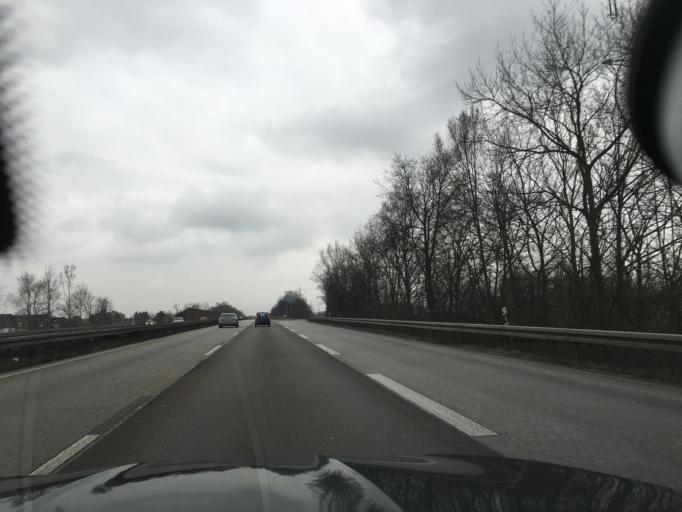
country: DE
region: North Rhine-Westphalia
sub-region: Regierungsbezirk Koln
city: Wahn-Heide
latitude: 50.8621
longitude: 7.0963
